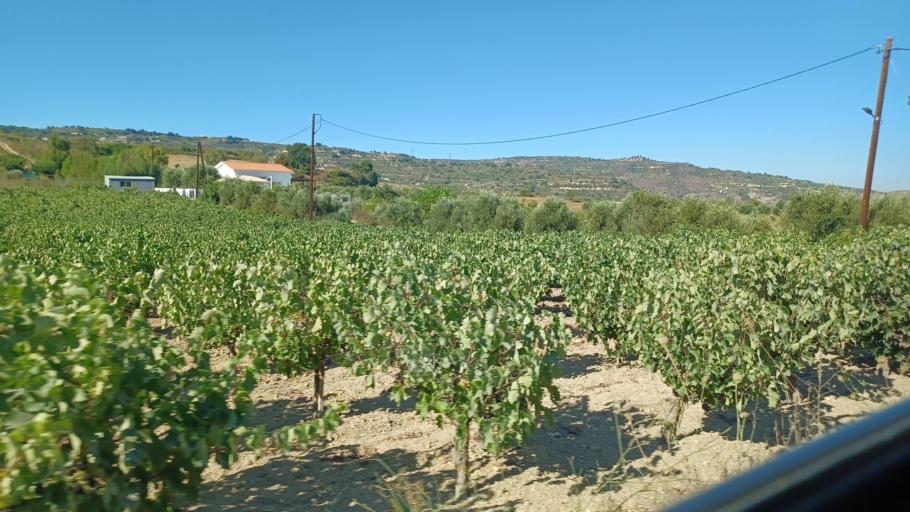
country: CY
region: Pafos
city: Mesogi
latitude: 34.8717
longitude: 32.5035
